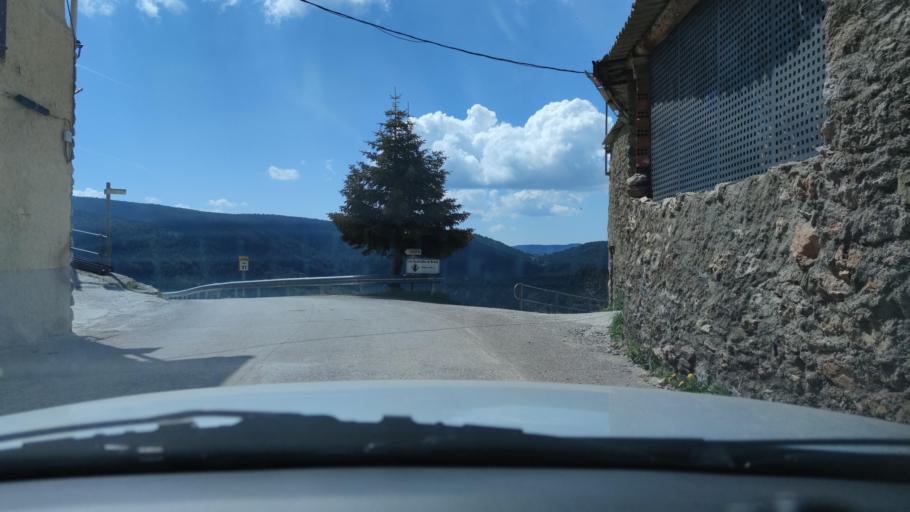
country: ES
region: Catalonia
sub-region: Provincia de Lleida
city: Coll de Nargo
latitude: 42.2859
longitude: 1.2343
